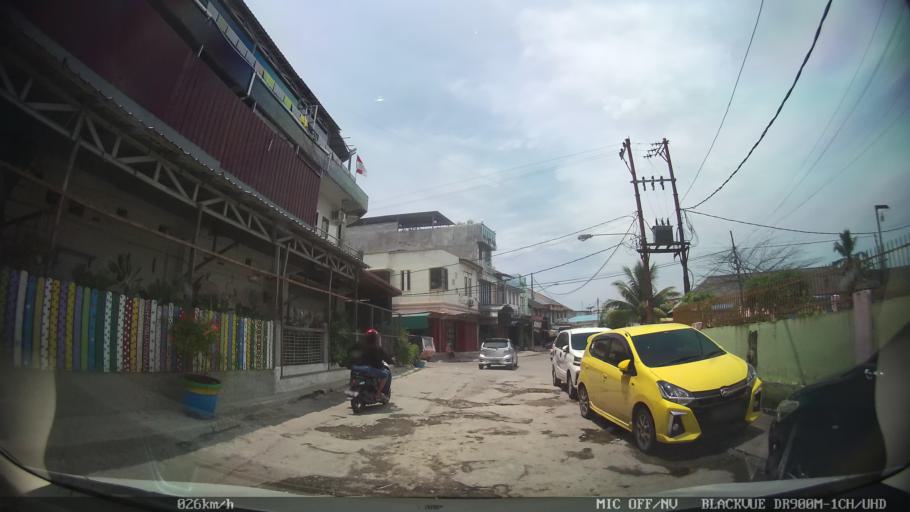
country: ID
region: North Sumatra
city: Belawan
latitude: 3.7842
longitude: 98.6883
